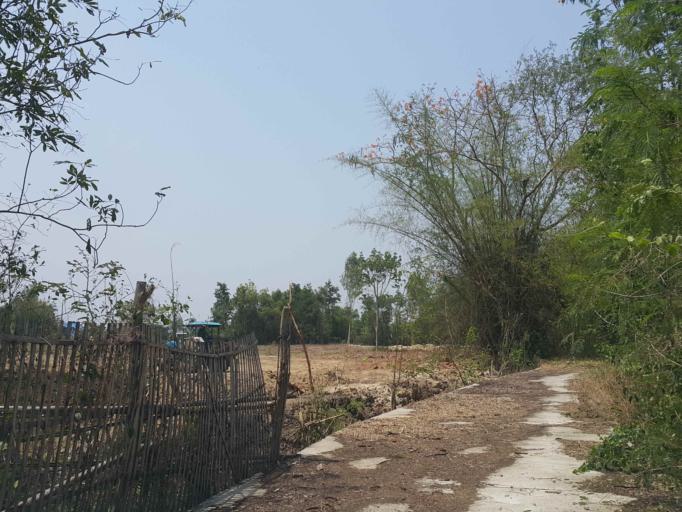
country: TH
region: Chiang Mai
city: San Kamphaeng
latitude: 18.7601
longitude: 99.0858
